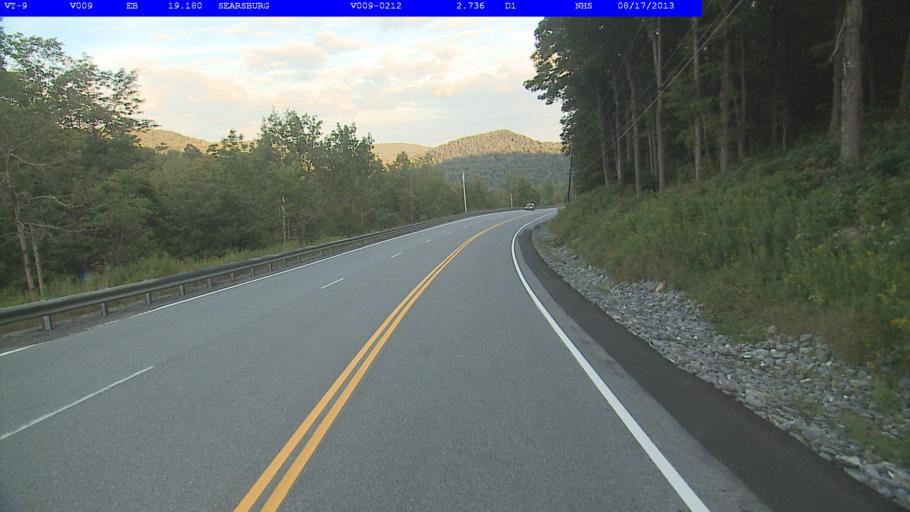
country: US
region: Vermont
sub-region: Windham County
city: Dover
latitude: 42.8967
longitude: -72.9595
